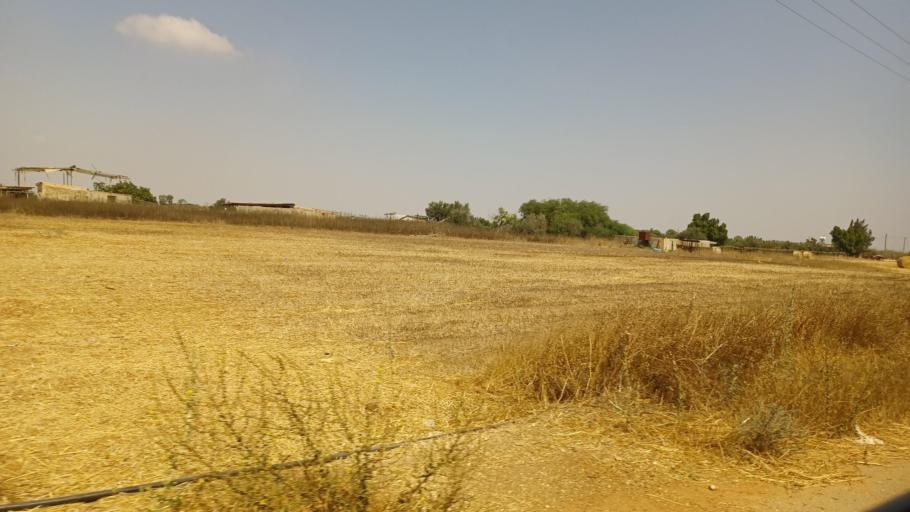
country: CY
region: Ammochostos
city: Frenaros
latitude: 35.0562
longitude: 33.9219
